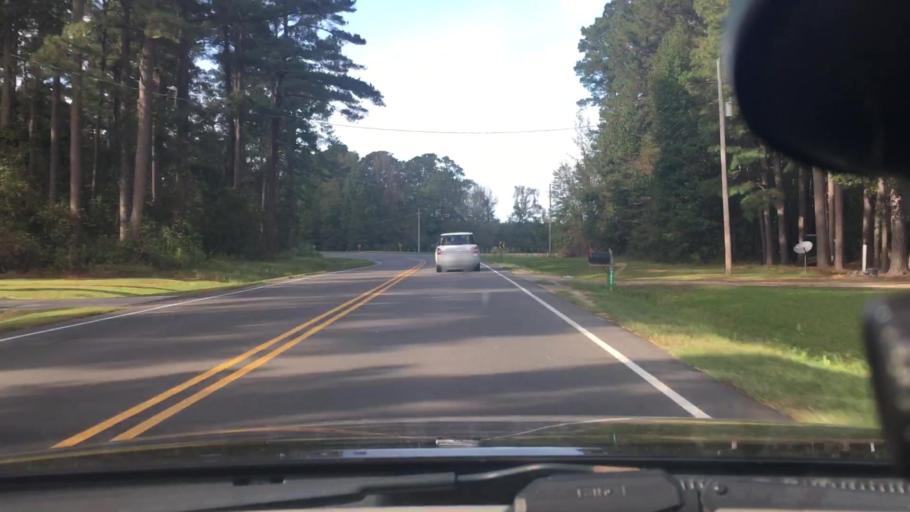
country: US
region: North Carolina
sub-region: Pitt County
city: Windsor
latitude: 35.4509
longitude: -77.2637
